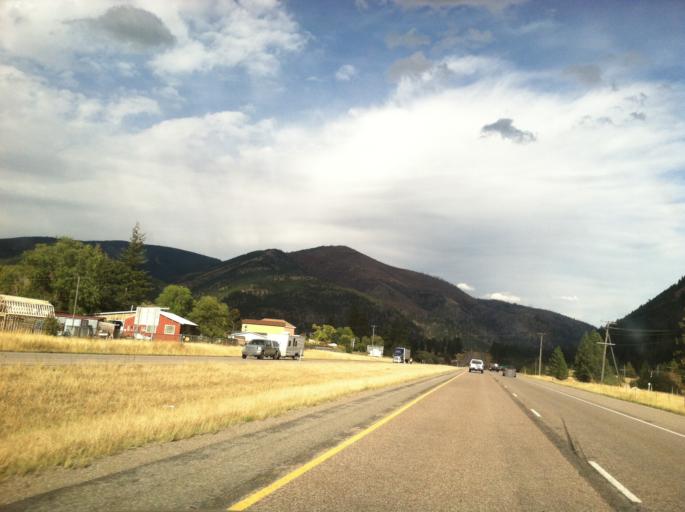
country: US
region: Montana
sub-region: Missoula County
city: East Missoula
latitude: 46.8686
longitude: -113.9429
